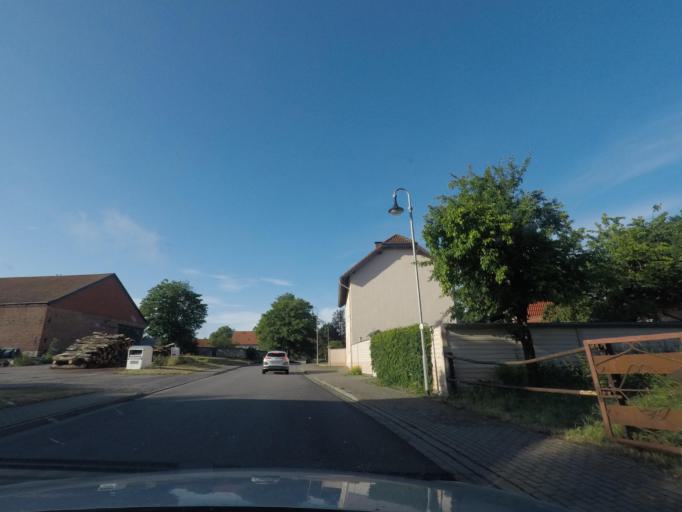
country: DE
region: Saxony-Anhalt
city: Huy-Neinstedt
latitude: 52.0121
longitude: 10.8980
